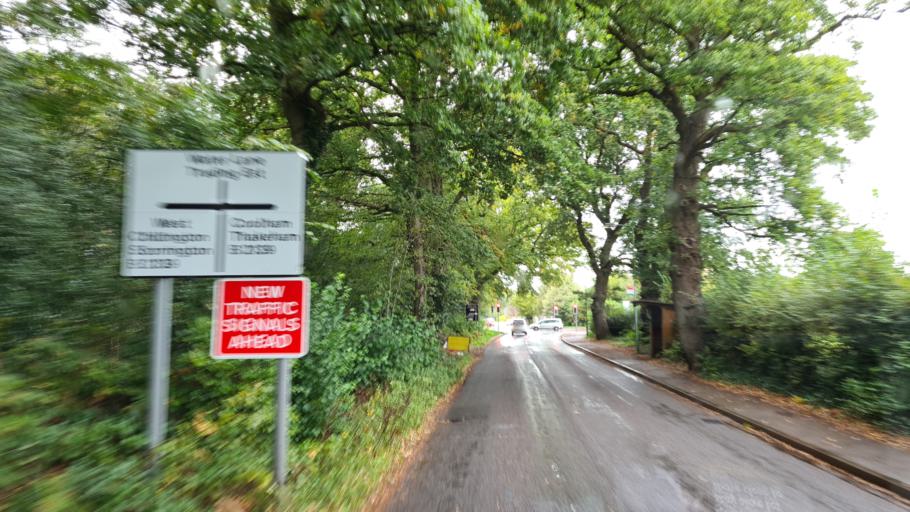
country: GB
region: England
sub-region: West Sussex
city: Storrington
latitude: 50.9223
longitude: -0.4384
